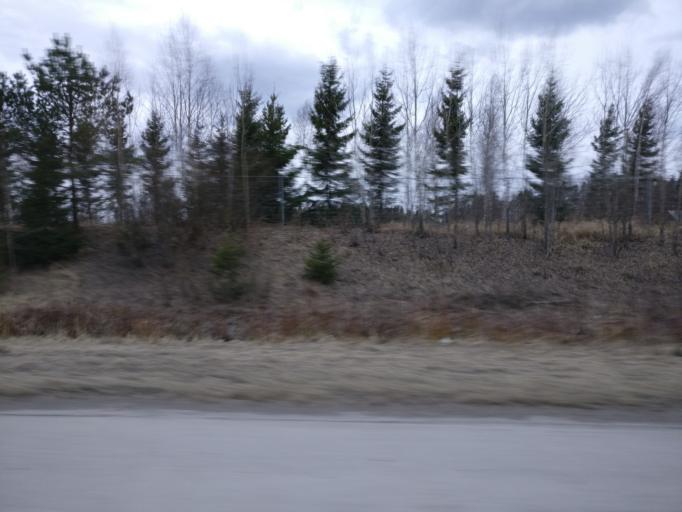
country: FI
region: Uusimaa
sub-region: Helsinki
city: Nurmijaervi
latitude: 60.5303
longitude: 24.8421
